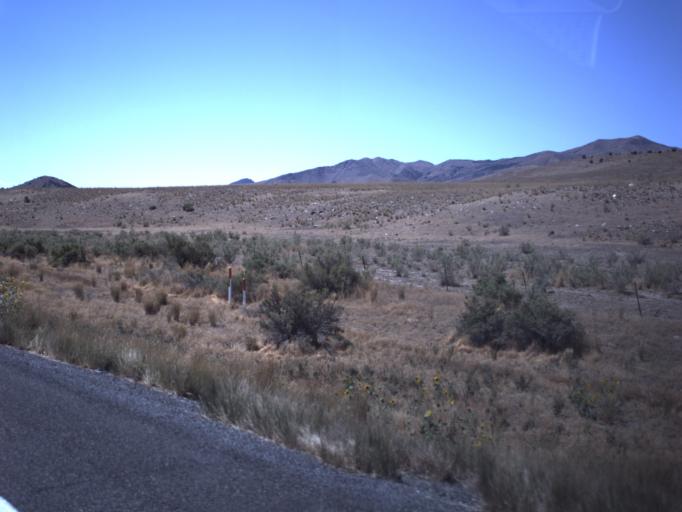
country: US
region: Utah
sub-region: Juab County
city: Nephi
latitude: 39.6254
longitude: -112.1225
